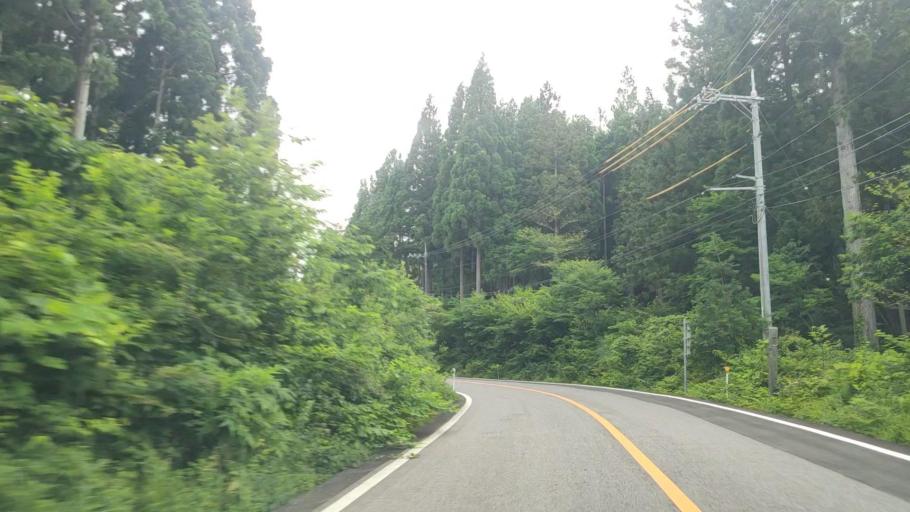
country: JP
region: Tottori
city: Yonago
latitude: 35.3326
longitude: 133.5570
